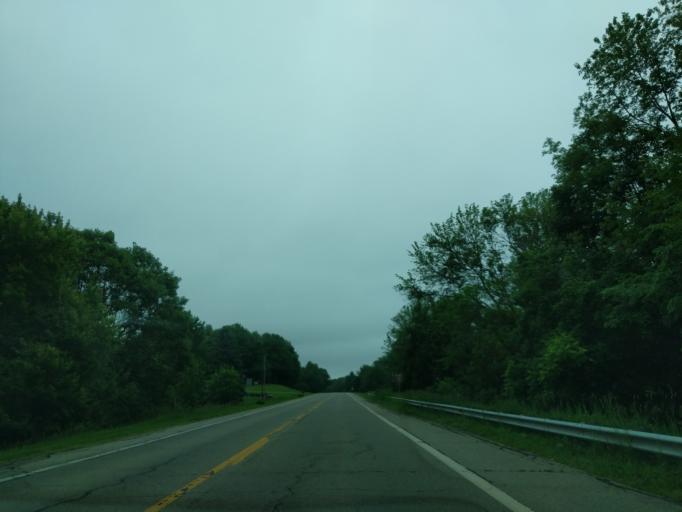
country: US
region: Michigan
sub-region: Hillsdale County
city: Litchfield
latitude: 42.0355
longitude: -84.7364
